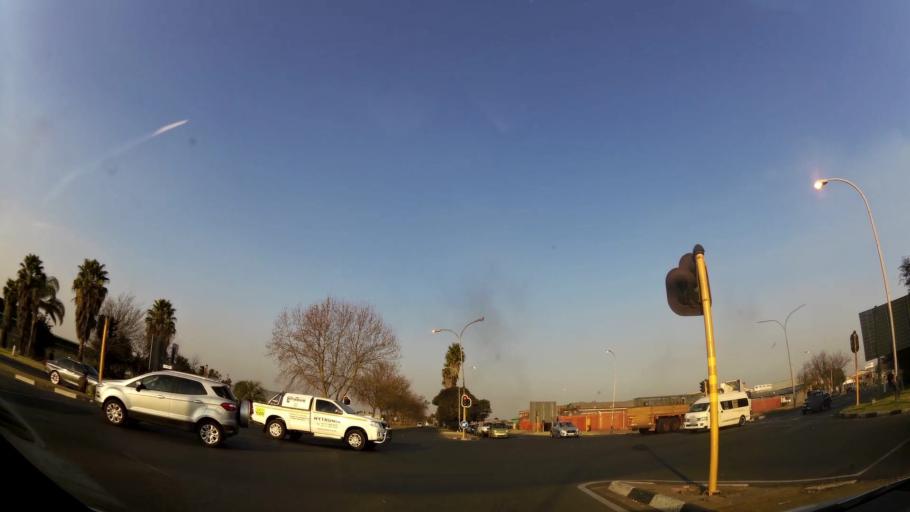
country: ZA
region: Gauteng
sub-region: Ekurhuleni Metropolitan Municipality
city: Springs
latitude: -26.2554
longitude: 28.4179
